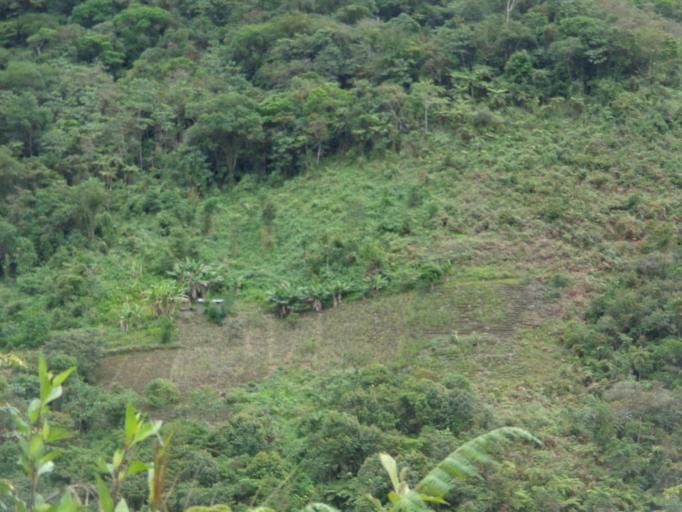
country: BO
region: La Paz
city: Coroico
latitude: -16.0466
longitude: -68.0045
